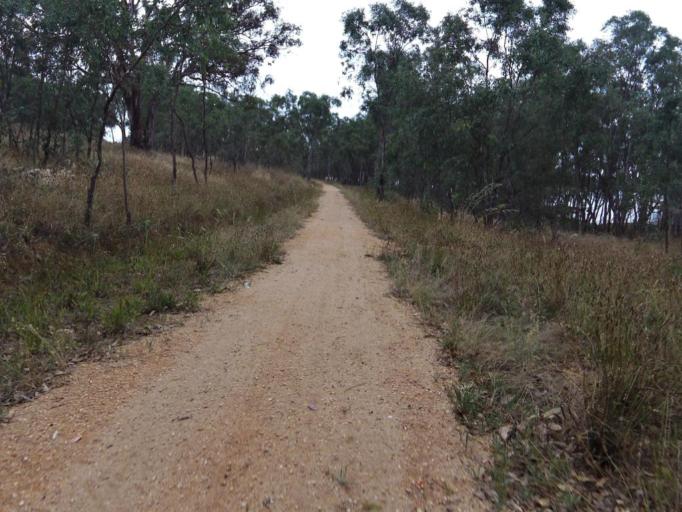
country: AU
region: Victoria
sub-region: Greater Bendigo
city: Kennington
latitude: -36.8651
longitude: 144.6230
